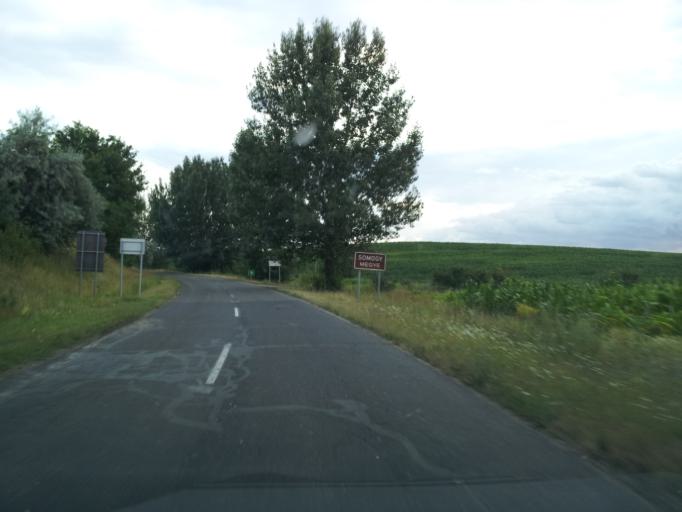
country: HU
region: Somogy
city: Adand
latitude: 46.8147
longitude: 18.1986
